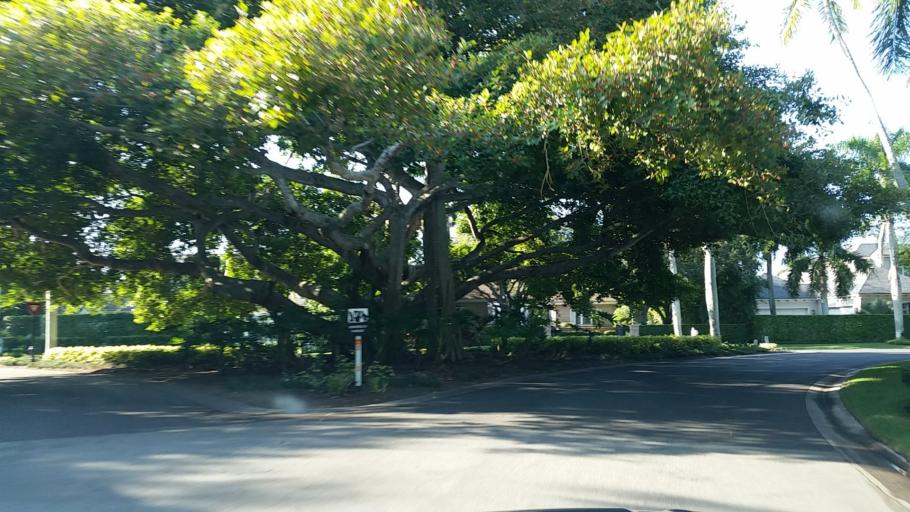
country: US
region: Florida
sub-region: Collier County
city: Naples
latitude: 26.1003
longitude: -81.7933
